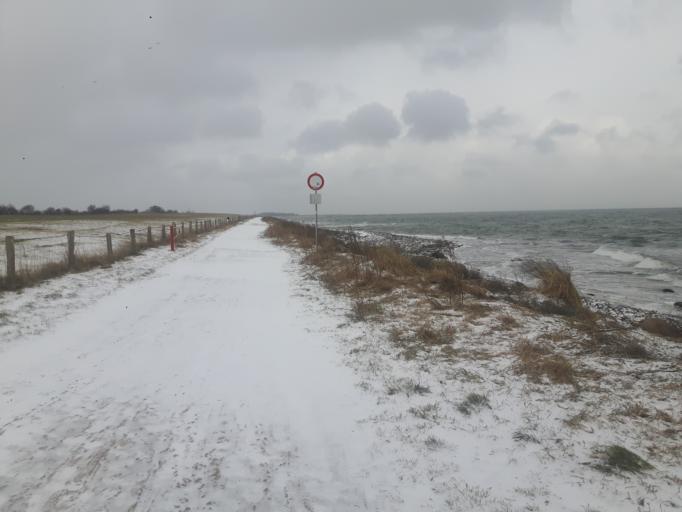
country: DE
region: Schleswig-Holstein
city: Fehmarn
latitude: 54.5043
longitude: 11.2170
